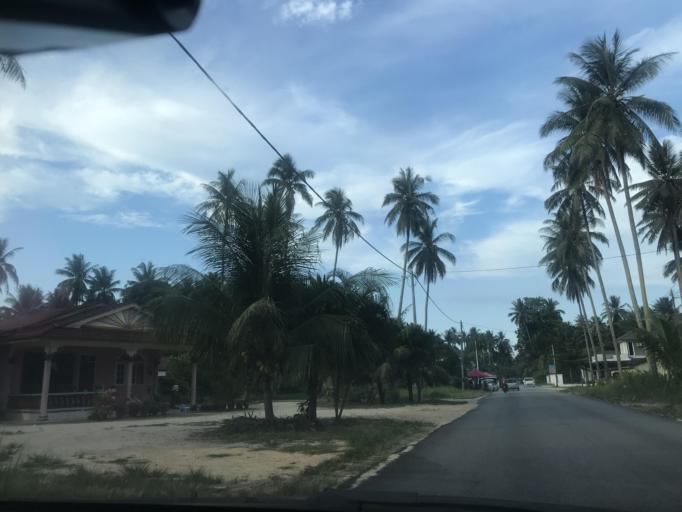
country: MY
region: Kelantan
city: Kota Bharu
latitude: 6.1290
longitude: 102.3604
